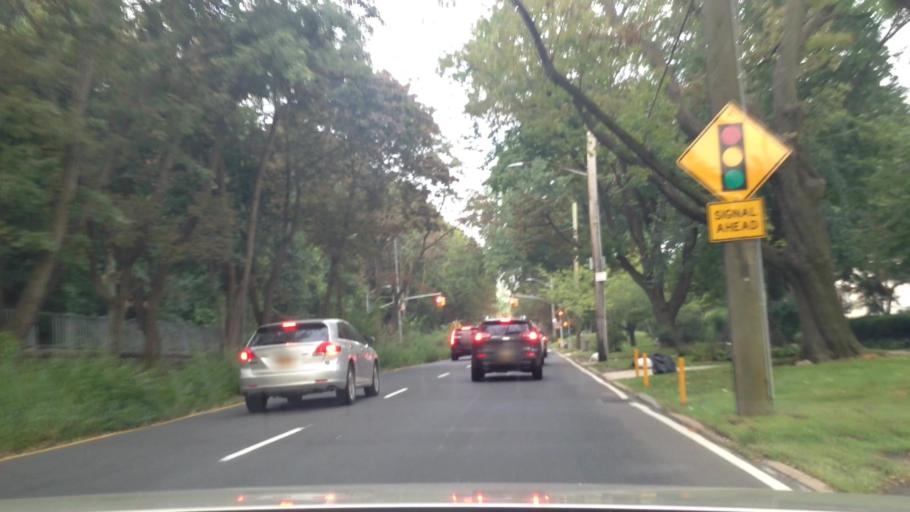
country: US
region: New York
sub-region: Queens County
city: Borough of Queens
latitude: 40.7108
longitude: -73.8386
